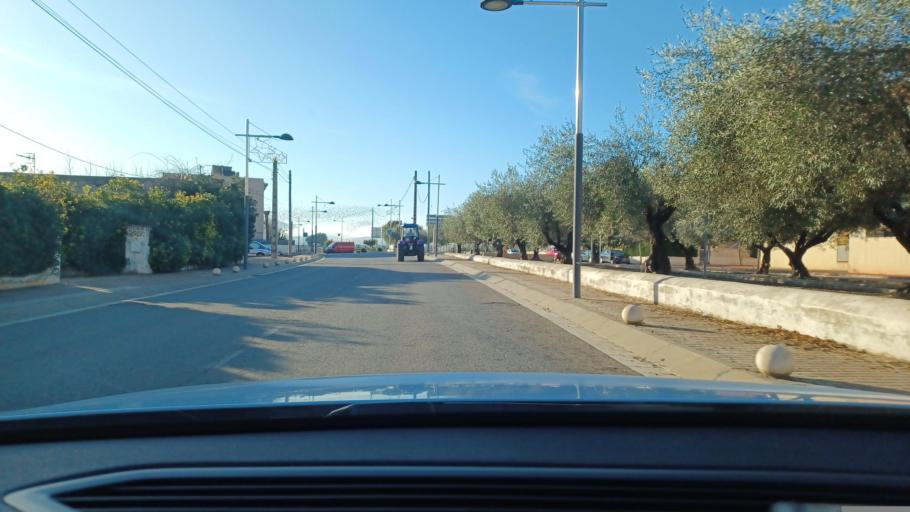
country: ES
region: Catalonia
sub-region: Provincia de Tarragona
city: Santa Barbara
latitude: 40.7137
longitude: 0.5016
